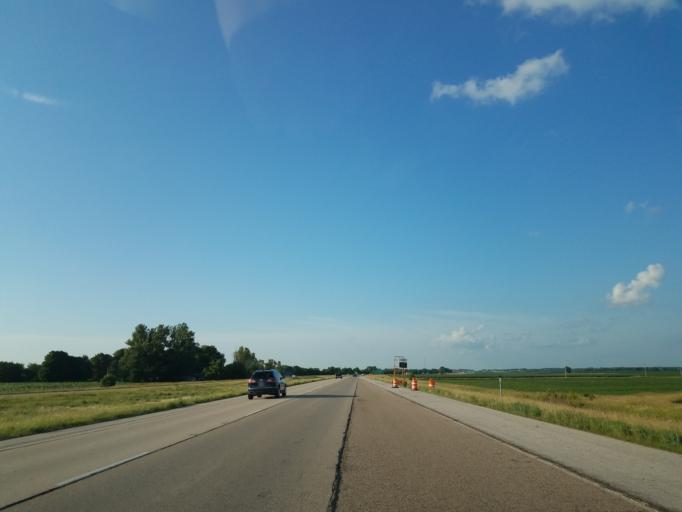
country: US
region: Illinois
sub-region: McLean County
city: Twin Grove
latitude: 40.4128
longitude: -89.0512
